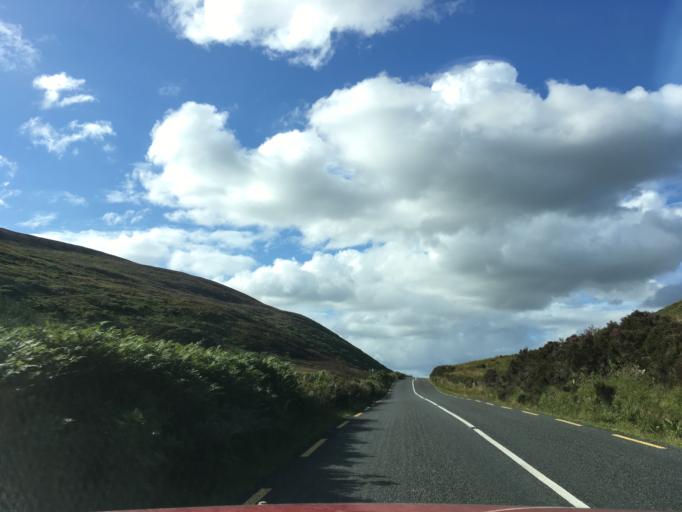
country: IE
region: Munster
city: Cahir
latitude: 52.2379
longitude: -7.9537
